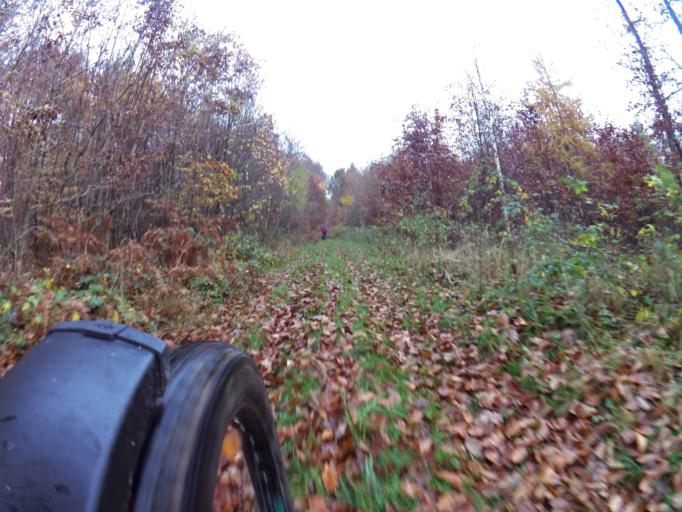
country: PL
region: Pomeranian Voivodeship
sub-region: Powiat pucki
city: Krokowa
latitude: 54.7329
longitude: 18.1314
